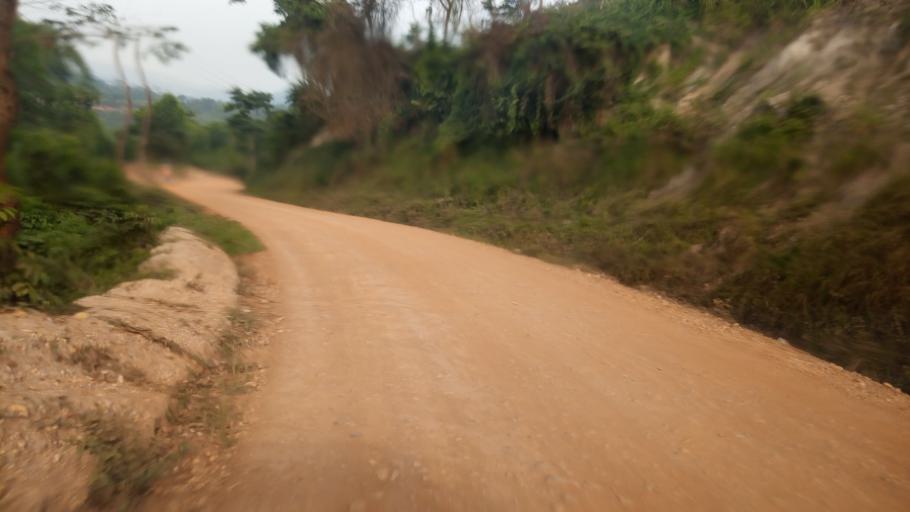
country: UG
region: Western Region
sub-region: Kanungu District
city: Ntungamo
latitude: -0.8388
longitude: 29.6468
